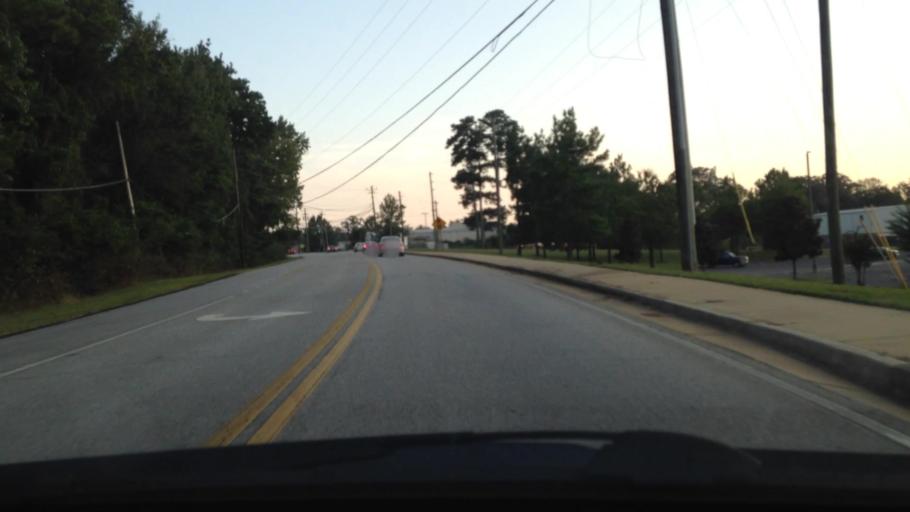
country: US
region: Alabama
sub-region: Russell County
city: Phenix City
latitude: 32.5589
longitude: -84.9734
